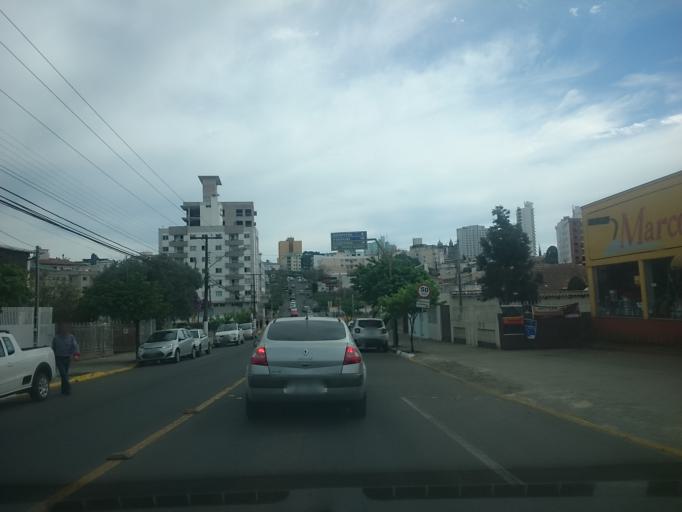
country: BR
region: Santa Catarina
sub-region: Lages
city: Lages
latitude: -27.8203
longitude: -50.3203
